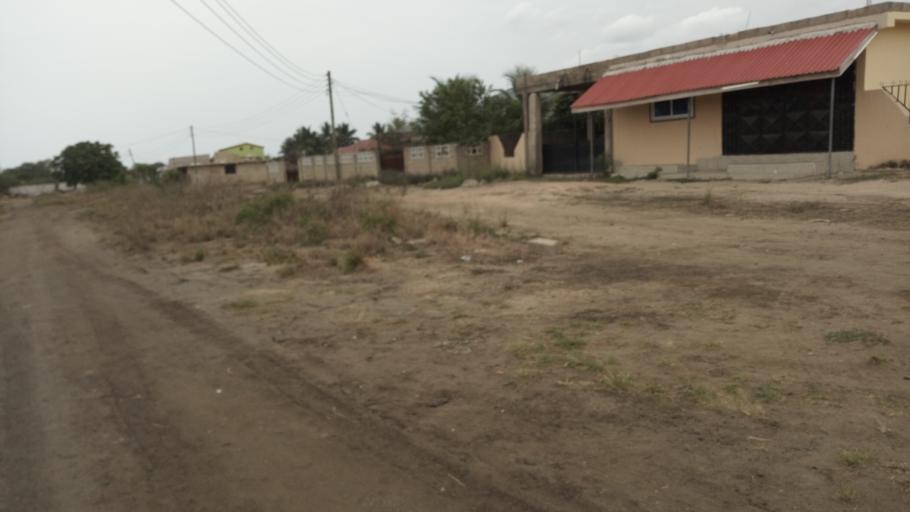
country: GH
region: Central
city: Winneba
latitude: 5.3747
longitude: -0.6335
